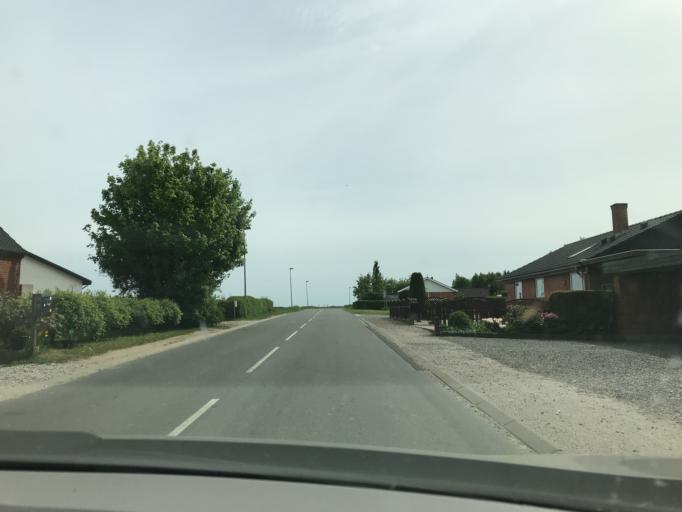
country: DK
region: Central Jutland
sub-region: Norddjurs Kommune
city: Allingabro
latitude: 56.5488
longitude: 10.2999
